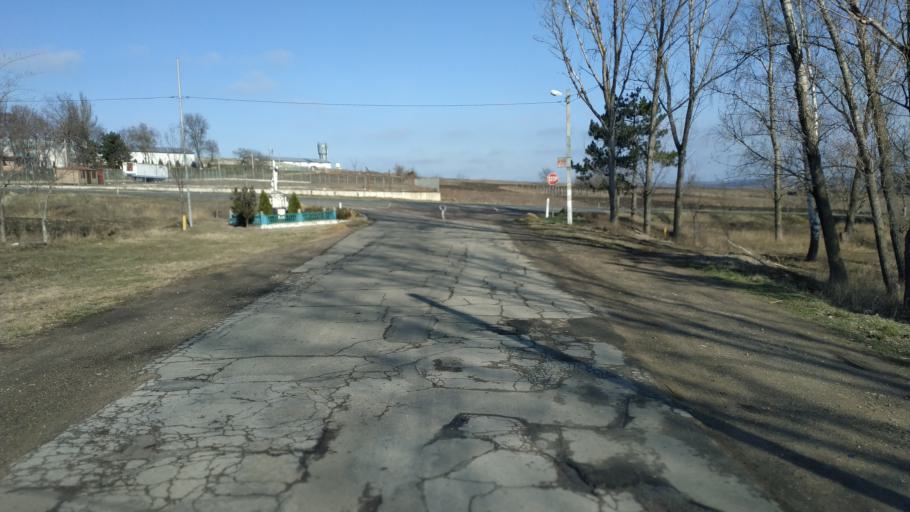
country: MD
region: Laloveni
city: Ialoveni
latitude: 46.9487
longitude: 28.7203
